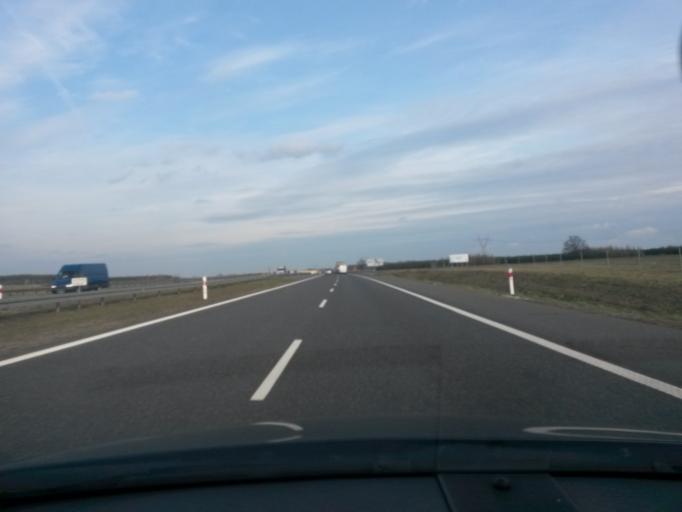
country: PL
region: Lodz Voivodeship
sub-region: Powiat zgierski
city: Ozorkow
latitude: 51.9301
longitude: 19.2900
